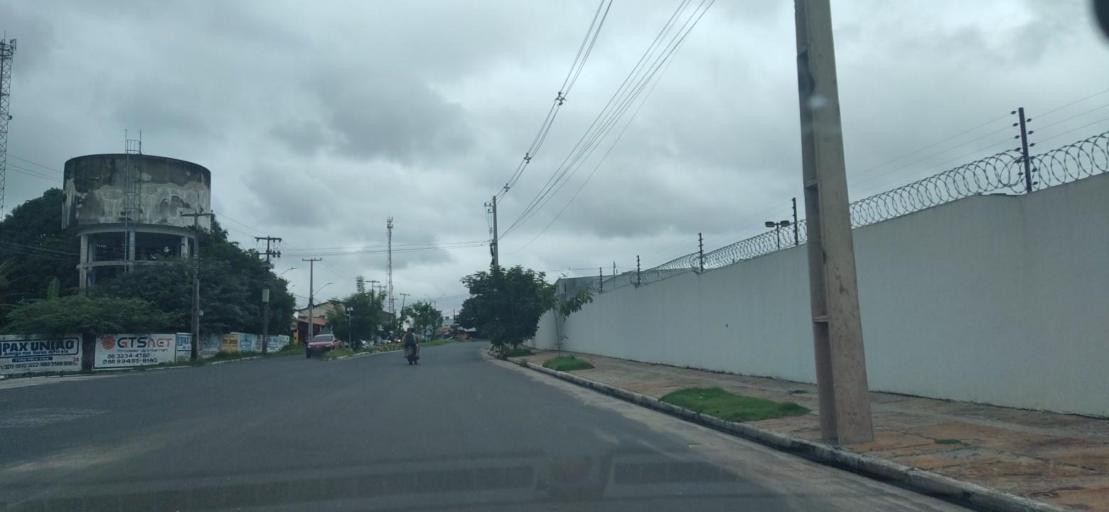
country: BR
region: Piaui
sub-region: Teresina
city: Teresina
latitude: -5.0507
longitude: -42.7400
